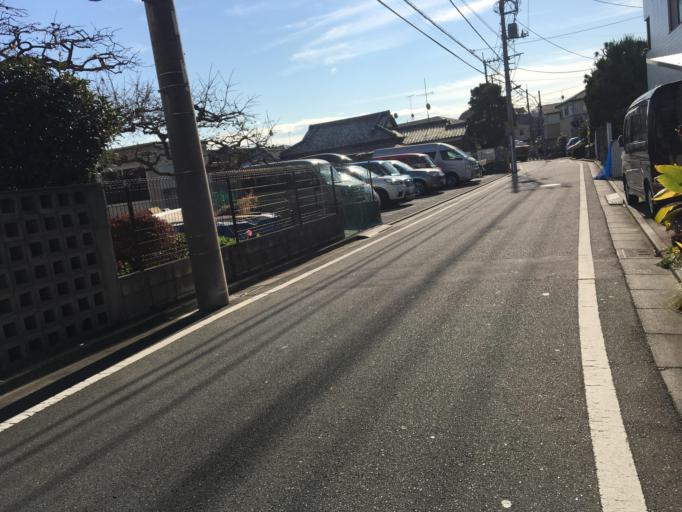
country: JP
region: Saitama
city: Wako
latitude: 35.7768
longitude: 139.6418
